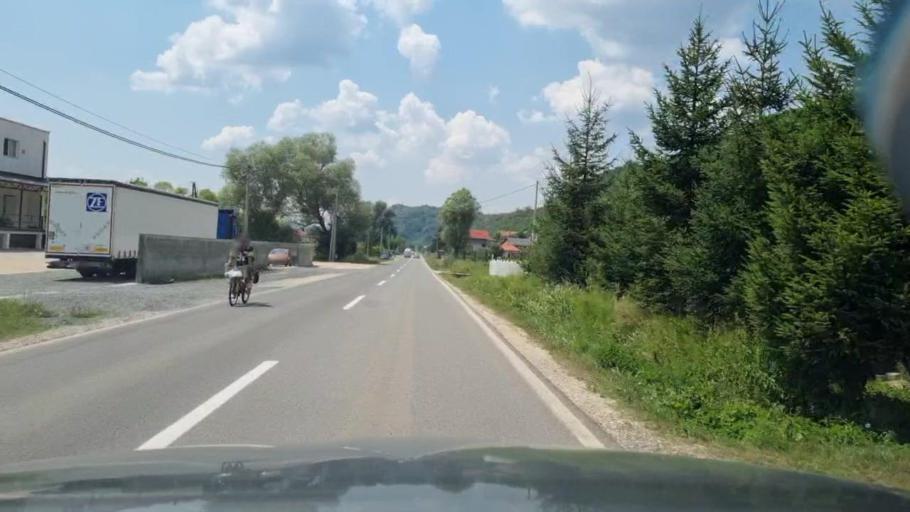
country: BA
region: Federation of Bosnia and Herzegovina
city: Gornja Tuzla
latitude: 44.5310
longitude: 18.7654
